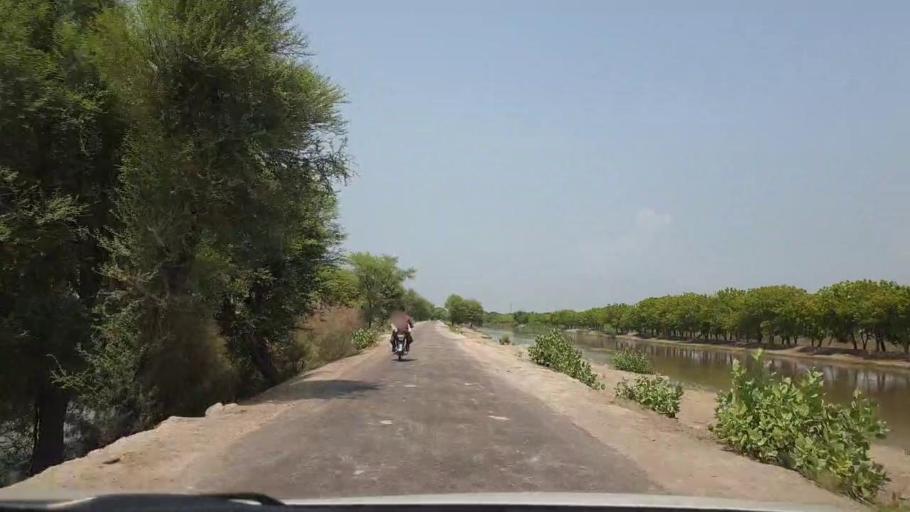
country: PK
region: Sindh
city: Dokri
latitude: 27.3530
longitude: 68.1127
